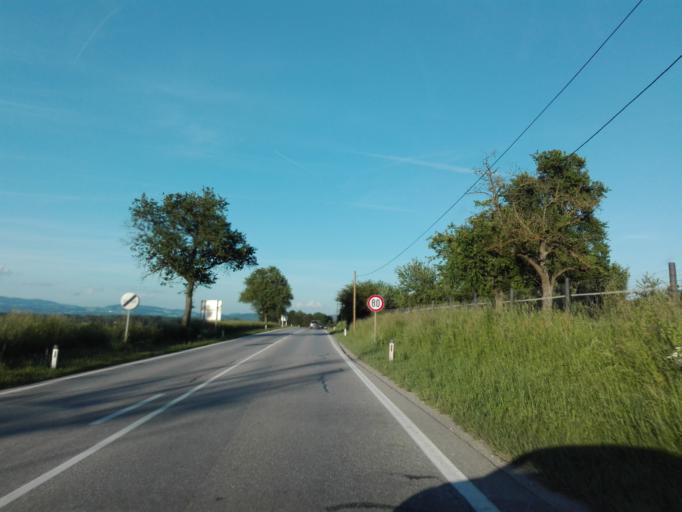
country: AT
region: Upper Austria
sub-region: Politischer Bezirk Urfahr-Umgebung
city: Feldkirchen an der Donau
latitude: 48.2904
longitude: 14.0489
